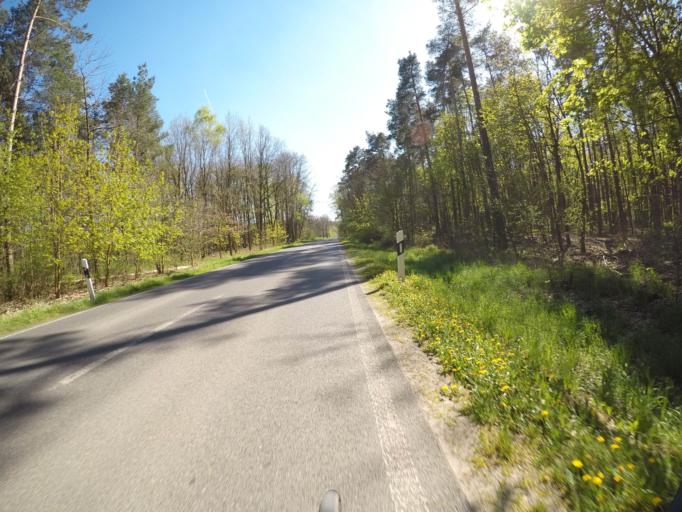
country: DE
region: Brandenburg
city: Rehfelde
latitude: 52.5487
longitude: 13.9397
